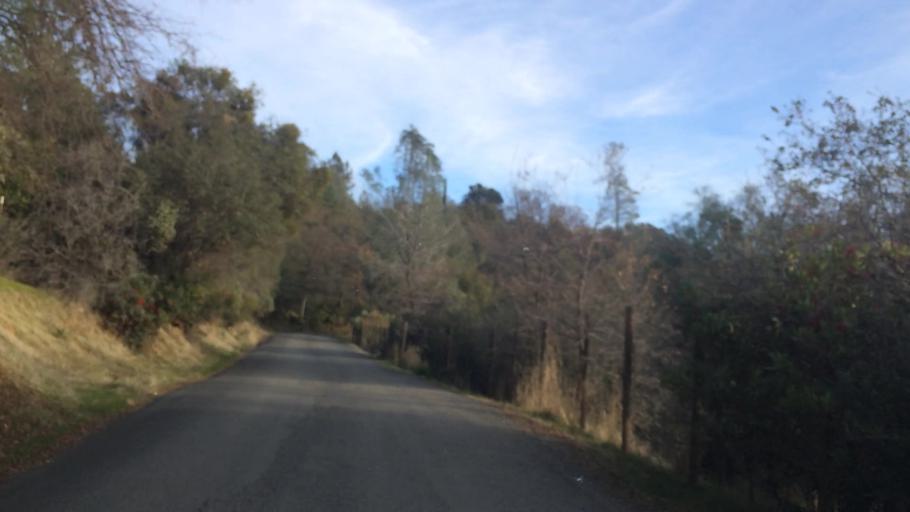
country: US
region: California
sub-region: Nevada County
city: Penn Valley
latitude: 39.2142
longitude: -121.1774
